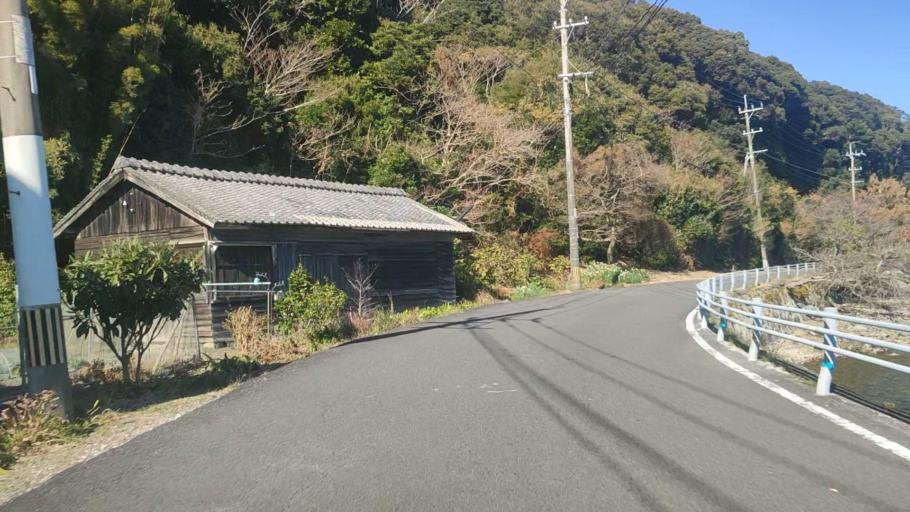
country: JP
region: Oita
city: Saiki
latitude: 32.8318
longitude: 131.9597
